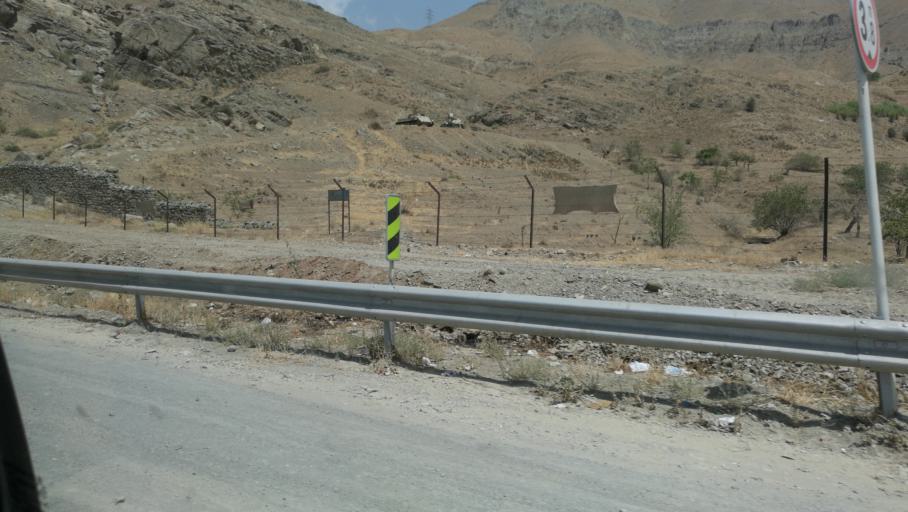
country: IR
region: Alborz
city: Karaj
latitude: 35.8270
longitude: 51.0420
